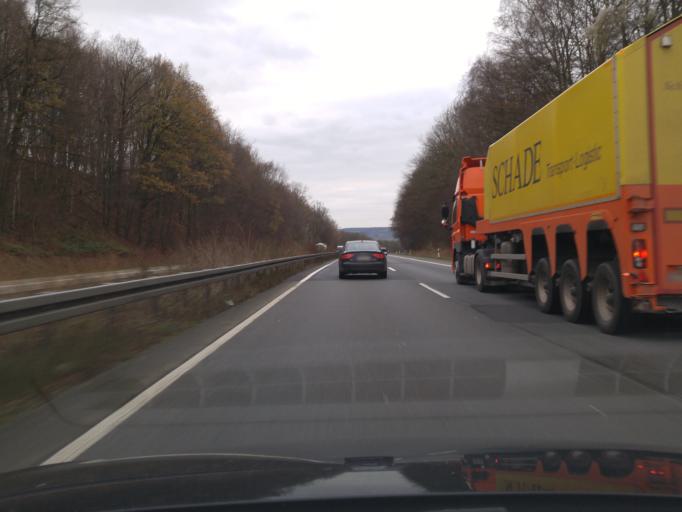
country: DE
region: Lower Saxony
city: Kalefeld
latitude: 51.8230
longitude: 10.1107
